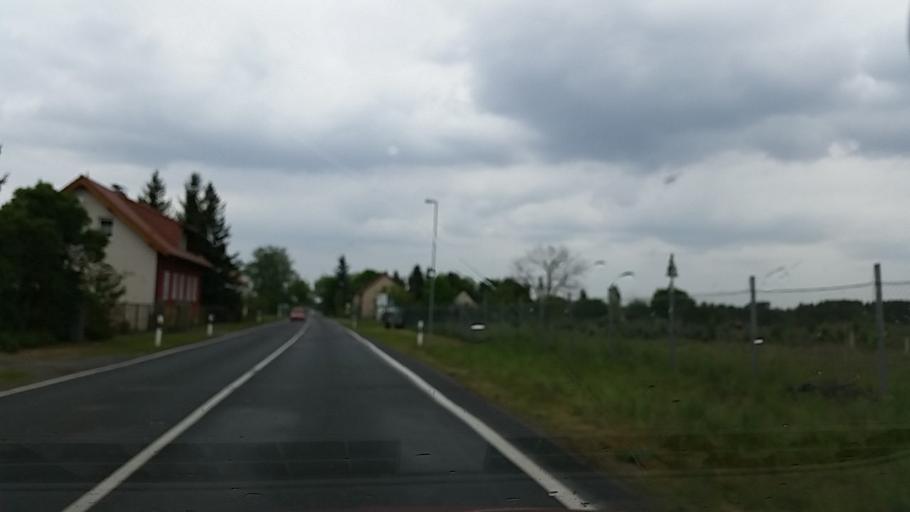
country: DE
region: Brandenburg
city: Spreenhagen
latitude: 52.3343
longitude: 13.8960
